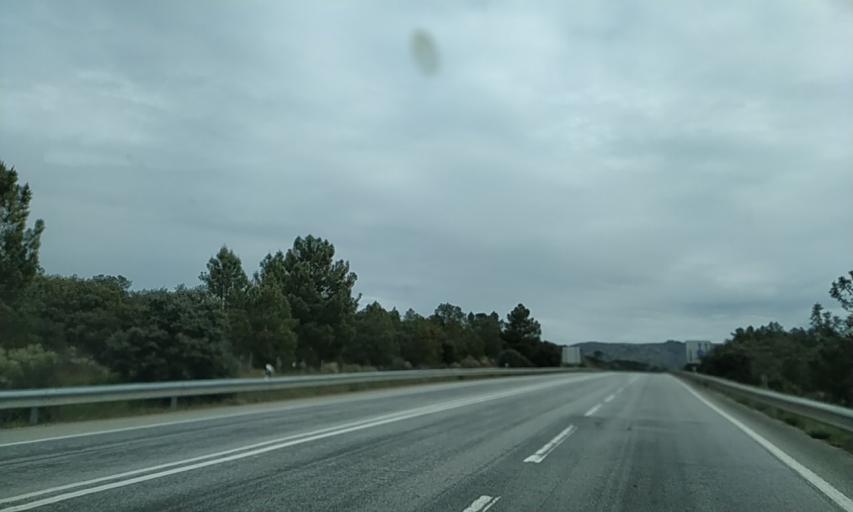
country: PT
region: Guarda
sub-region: Celorico da Beira
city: Celorico da Beira
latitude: 40.6323
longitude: -7.3131
